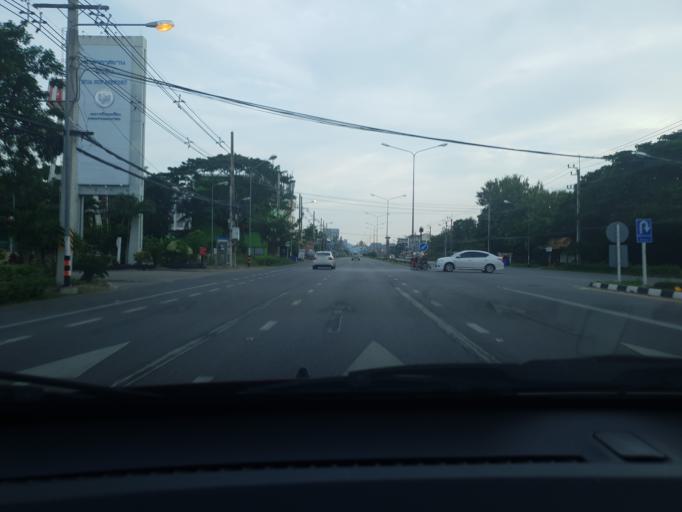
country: TH
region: Prachuap Khiri Khan
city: Hua Hin
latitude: 12.6271
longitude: 99.9509
